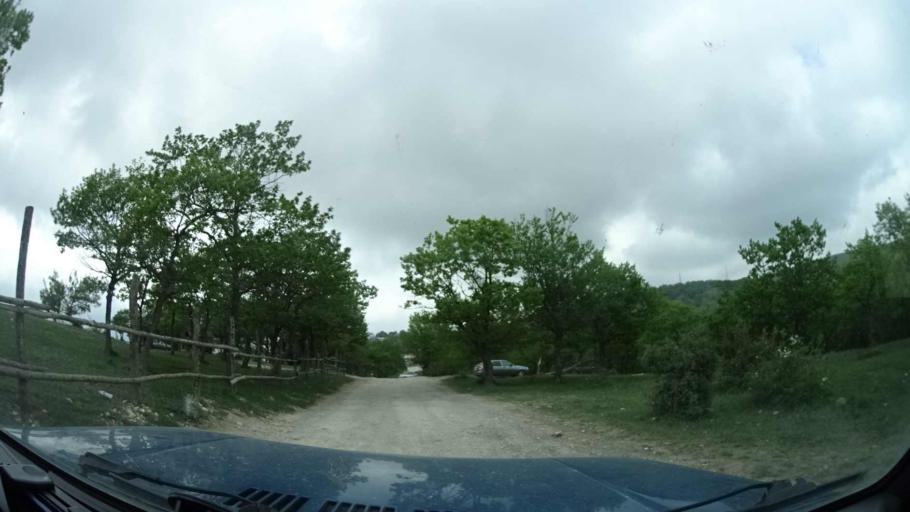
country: RU
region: Dagestan
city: Dubki
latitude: 43.0202
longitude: 46.8316
